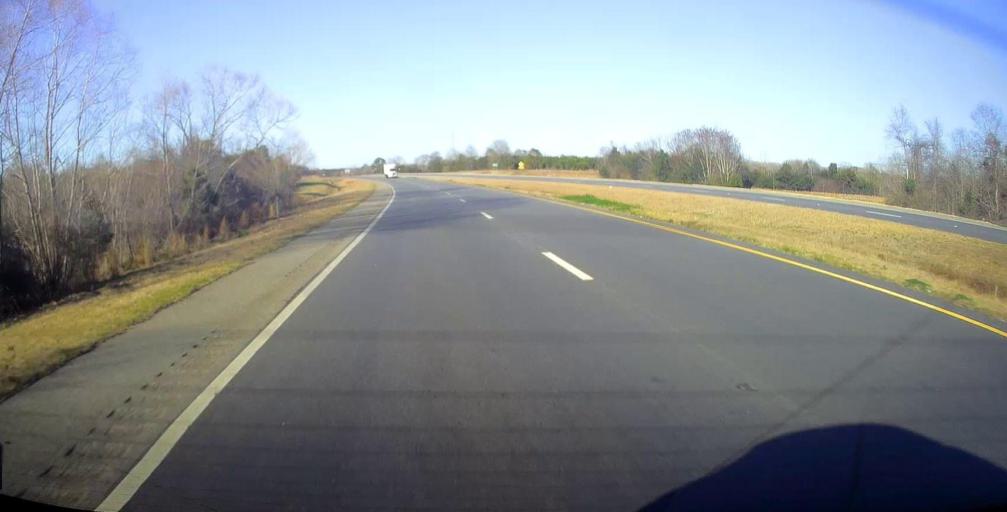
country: US
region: Georgia
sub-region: Sumter County
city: Americus
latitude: 31.9077
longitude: -84.2605
